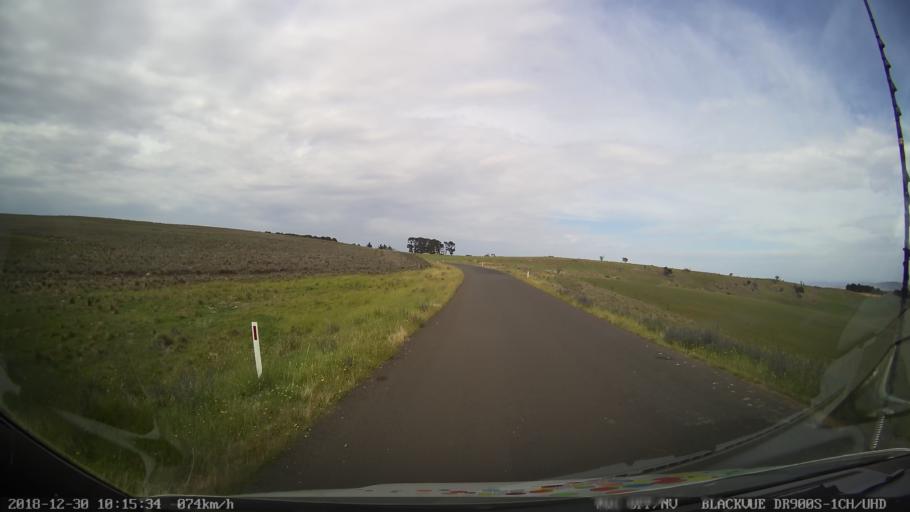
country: AU
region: New South Wales
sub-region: Snowy River
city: Berridale
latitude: -36.5437
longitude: 149.0444
